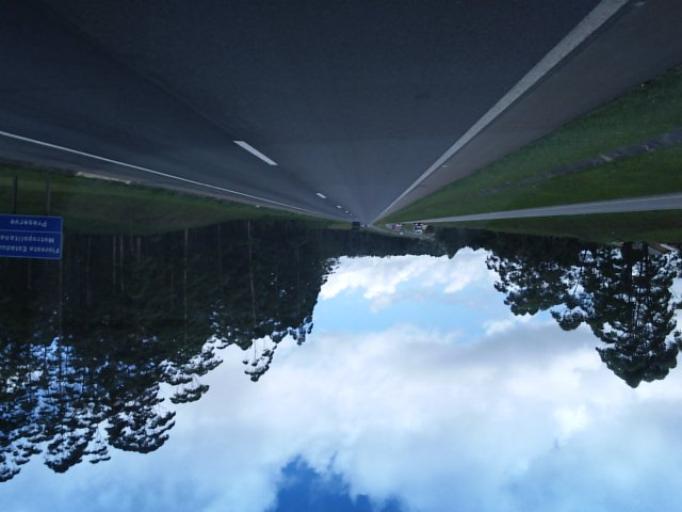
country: BR
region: Parana
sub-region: Piraquara
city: Piraquara
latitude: -25.4283
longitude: -49.0803
